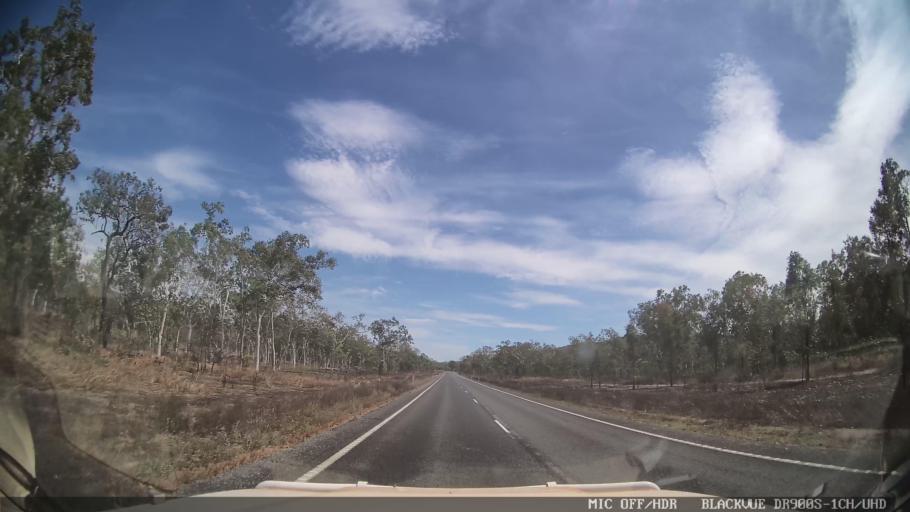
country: AU
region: Queensland
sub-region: Cook
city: Cooktown
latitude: -15.6942
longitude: 145.1303
